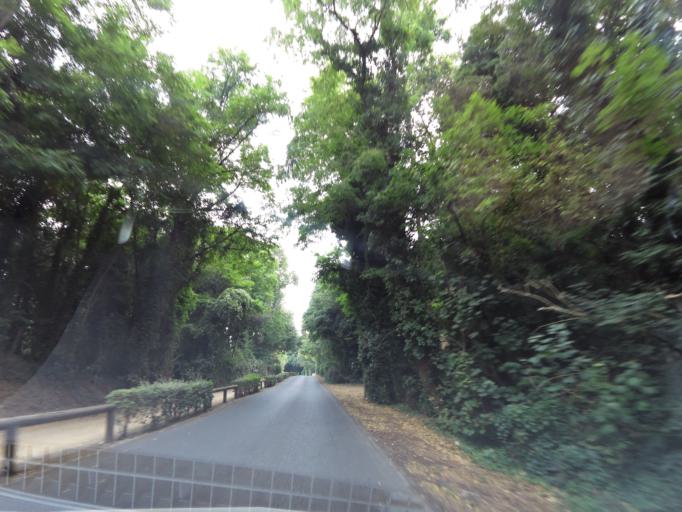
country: FR
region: Pays de la Loire
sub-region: Departement de la Vendee
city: Longeville-sur-Mer
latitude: 46.4037
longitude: -1.4995
